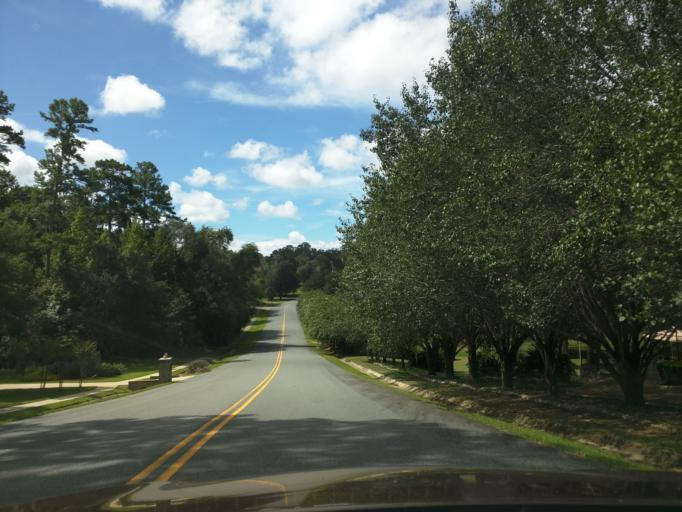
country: US
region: Florida
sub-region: Leon County
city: Tallahassee
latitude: 30.5758
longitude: -84.2597
